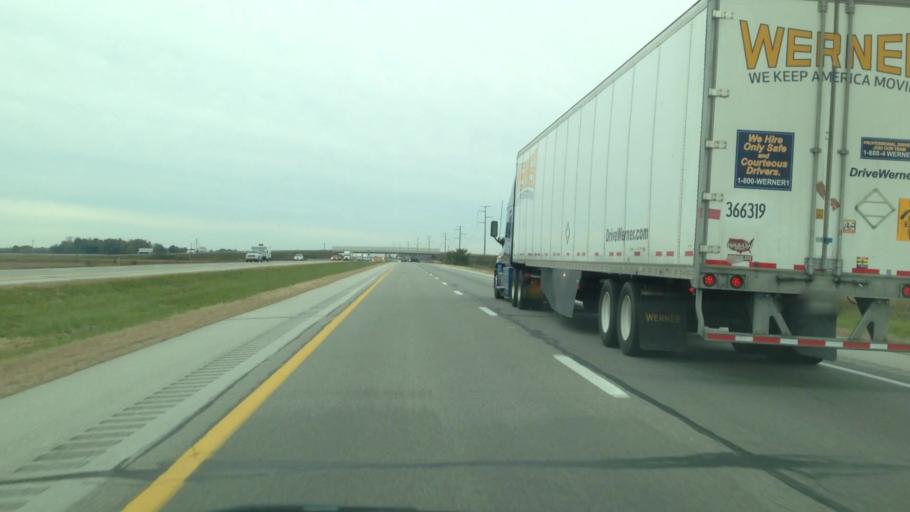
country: US
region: Ohio
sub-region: Fulton County
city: Swanton
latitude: 41.5999
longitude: -83.9339
